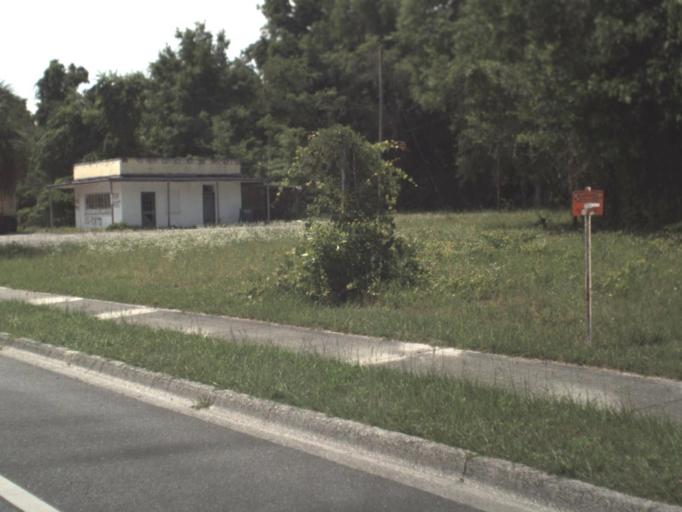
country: US
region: Florida
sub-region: Levy County
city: Chiefland
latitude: 29.4697
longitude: -82.8571
